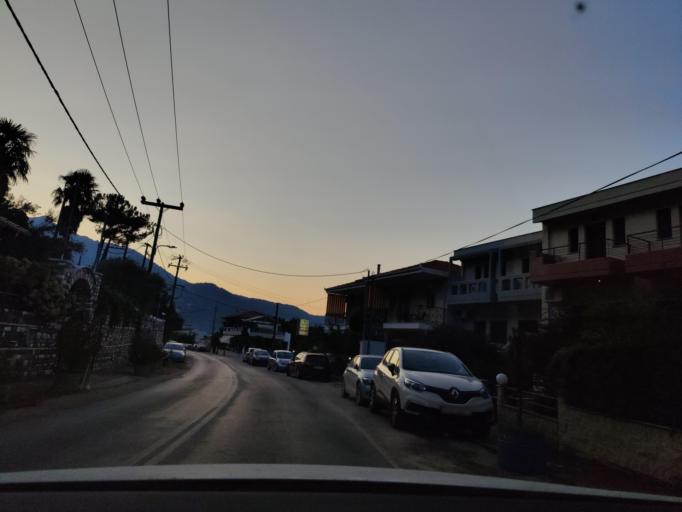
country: GR
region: East Macedonia and Thrace
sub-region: Nomos Kavalas
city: Potamia
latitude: 40.7062
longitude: 24.7612
